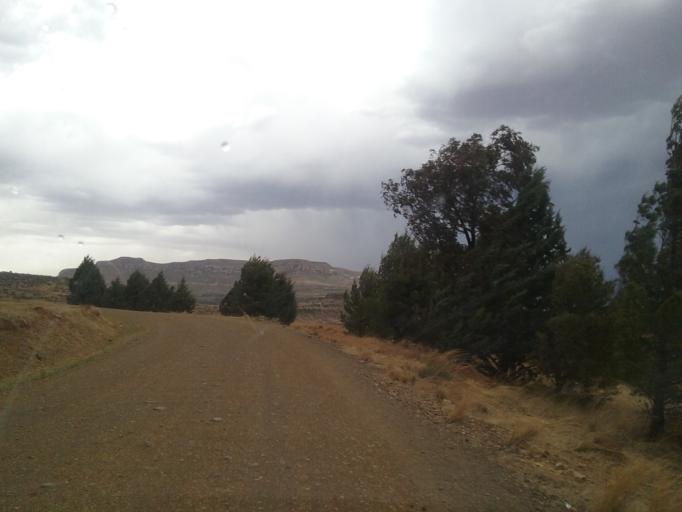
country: LS
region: Quthing
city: Quthing
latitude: -30.2960
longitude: 27.8160
